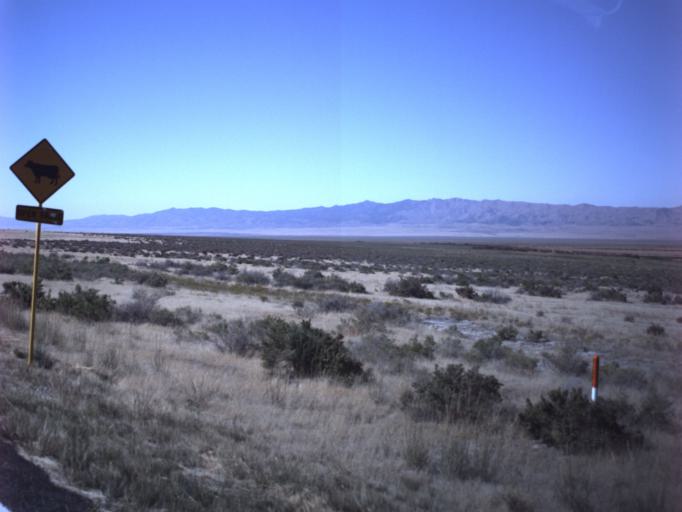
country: US
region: Utah
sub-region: Tooele County
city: Grantsville
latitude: 40.6103
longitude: -112.7063
